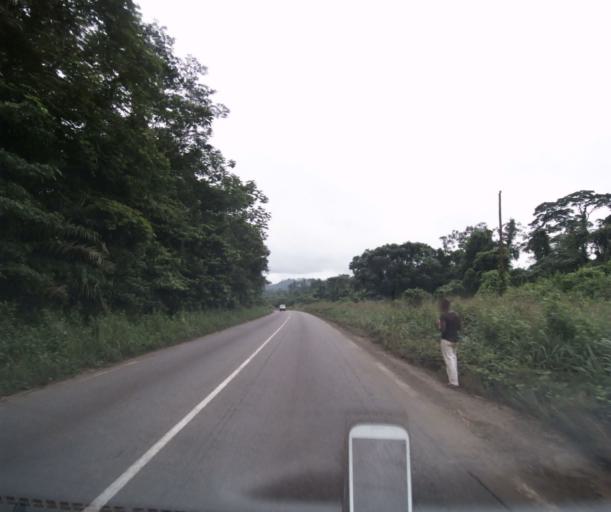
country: CM
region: Littoral
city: Edea
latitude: 3.8064
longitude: 10.2578
